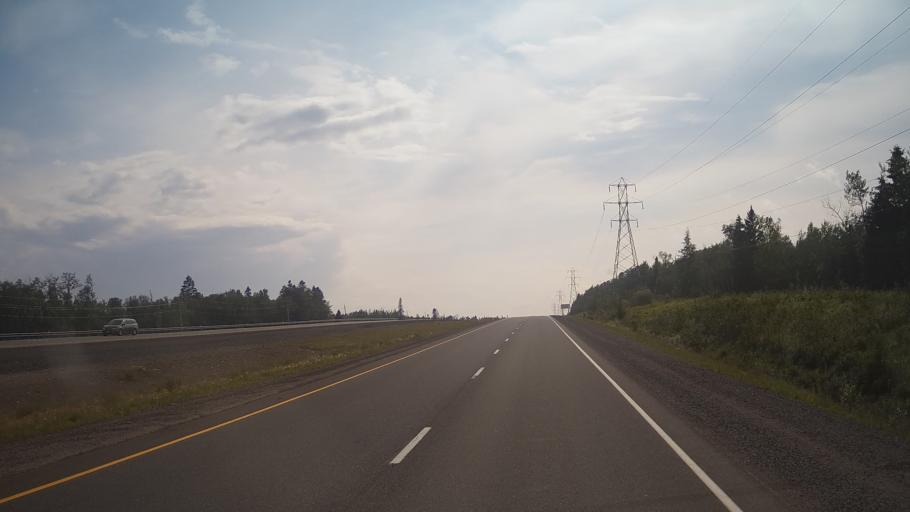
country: CA
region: Ontario
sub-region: Thunder Bay District
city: Thunder Bay
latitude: 48.5737
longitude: -88.8244
